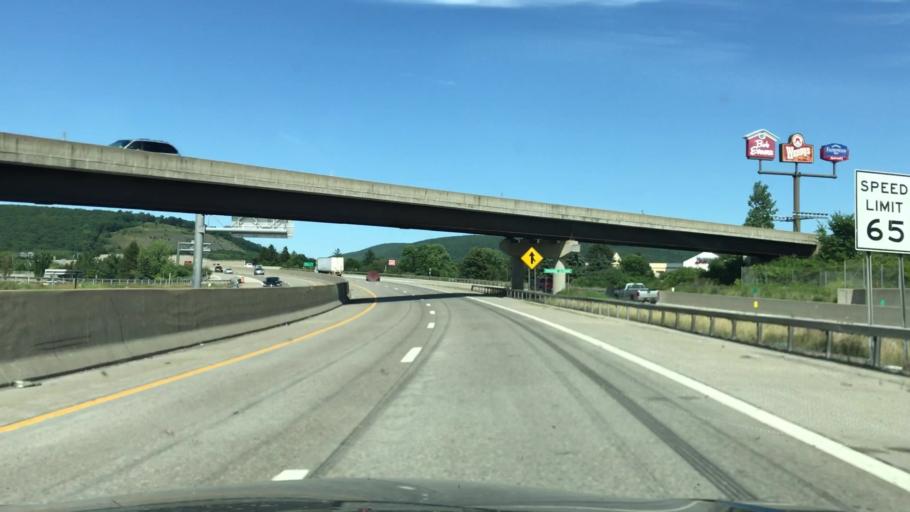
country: US
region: New York
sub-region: Steuben County
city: Painted Post
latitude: 42.1532
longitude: -77.0826
